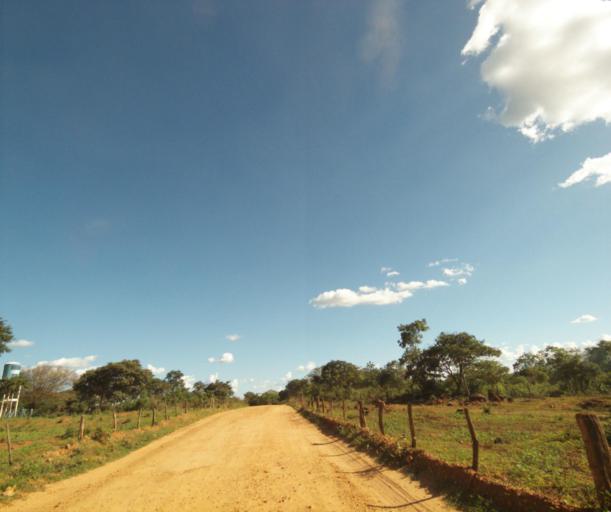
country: BR
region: Bahia
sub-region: Carinhanha
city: Carinhanha
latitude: -14.2086
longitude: -44.5410
